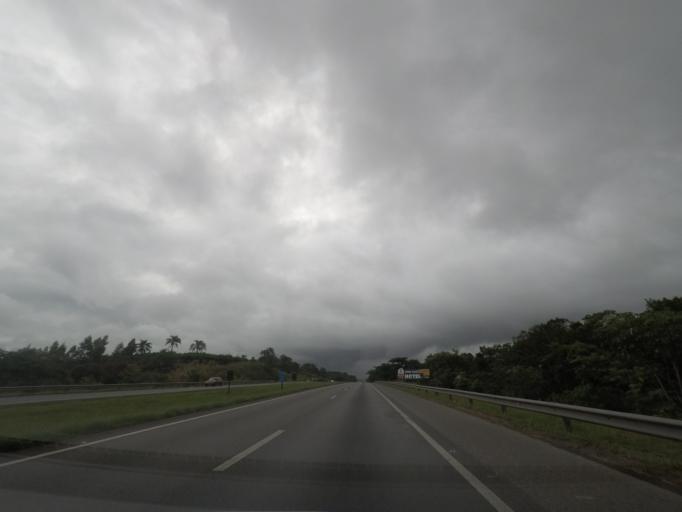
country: BR
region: Sao Paulo
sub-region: Registro
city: Registro
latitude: -24.5548
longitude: -47.8650
